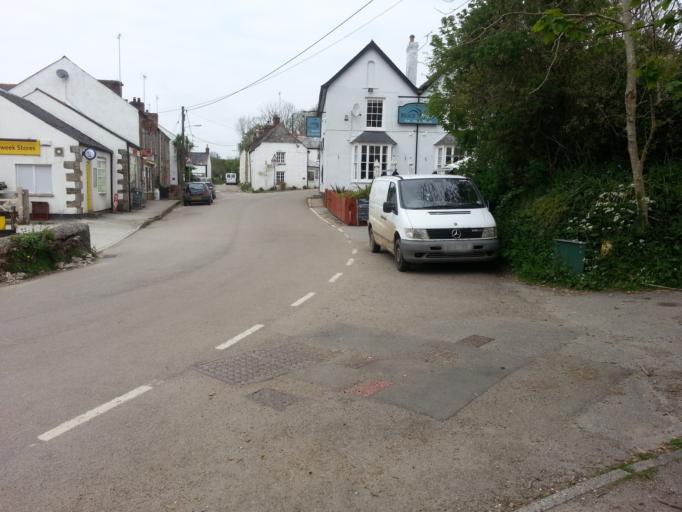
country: GB
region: England
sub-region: Cornwall
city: Wendron
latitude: 50.0968
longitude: -5.2080
